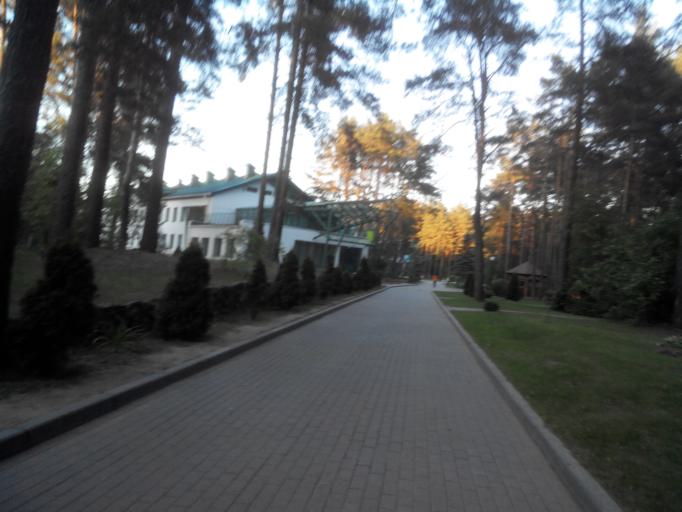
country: BY
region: Minsk
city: Narach
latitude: 54.8365
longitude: 26.7120
